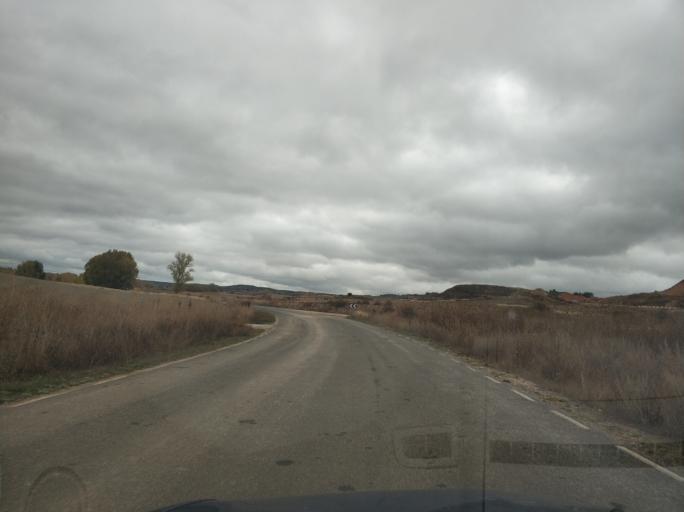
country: ES
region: Castille and Leon
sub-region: Provincia de Soria
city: San Esteban de Gormaz
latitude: 41.5811
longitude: -3.2041
